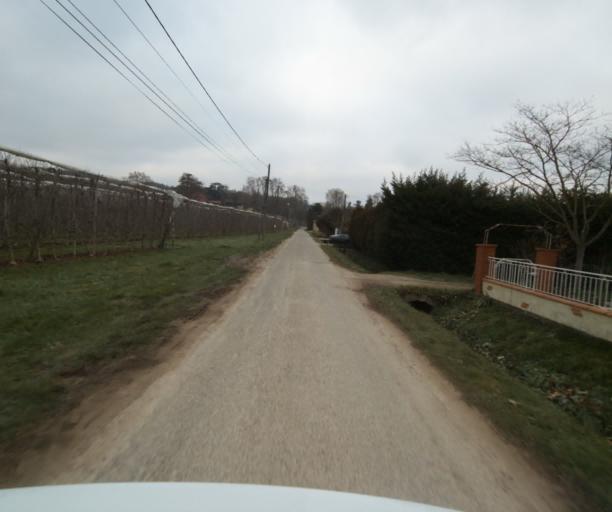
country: FR
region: Midi-Pyrenees
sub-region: Departement du Tarn-et-Garonne
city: Moissac
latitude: 44.1197
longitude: 1.1460
